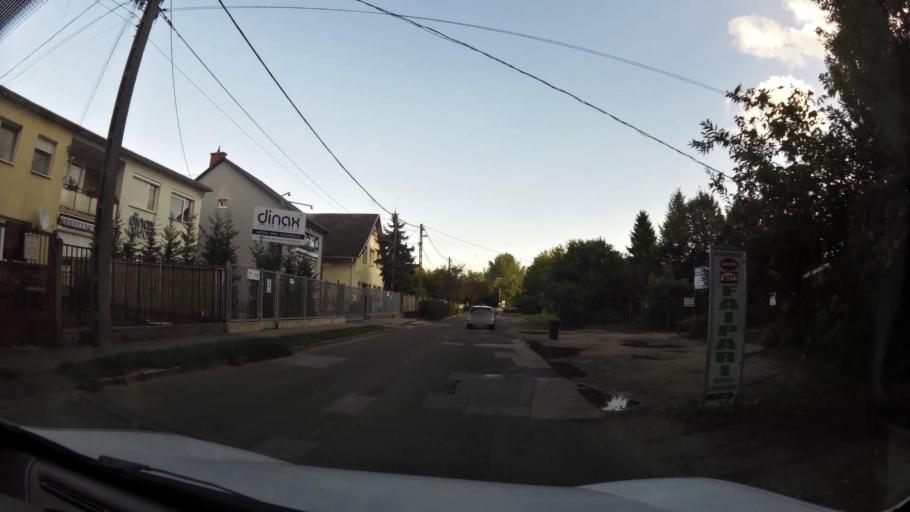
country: HU
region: Budapest
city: Budapest XVI. keruelet
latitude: 47.5039
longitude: 19.1700
